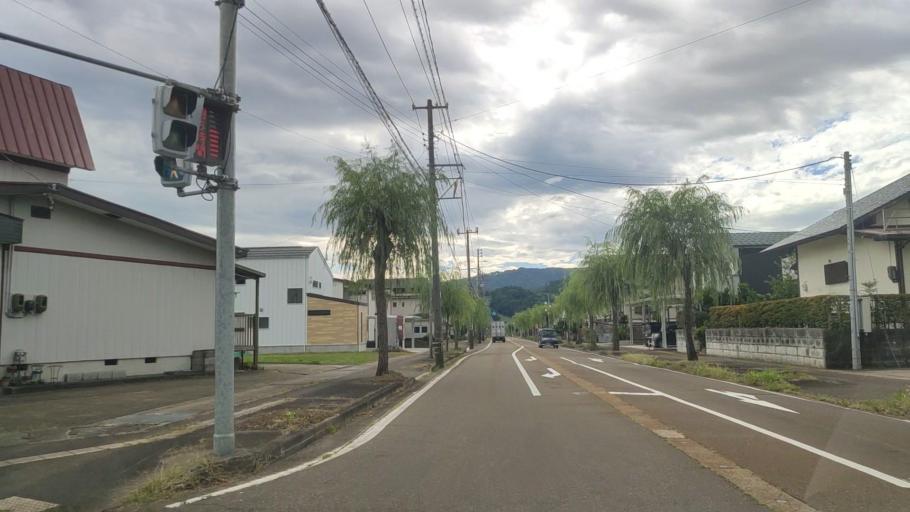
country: JP
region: Niigata
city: Arai
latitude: 37.0194
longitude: 138.2475
